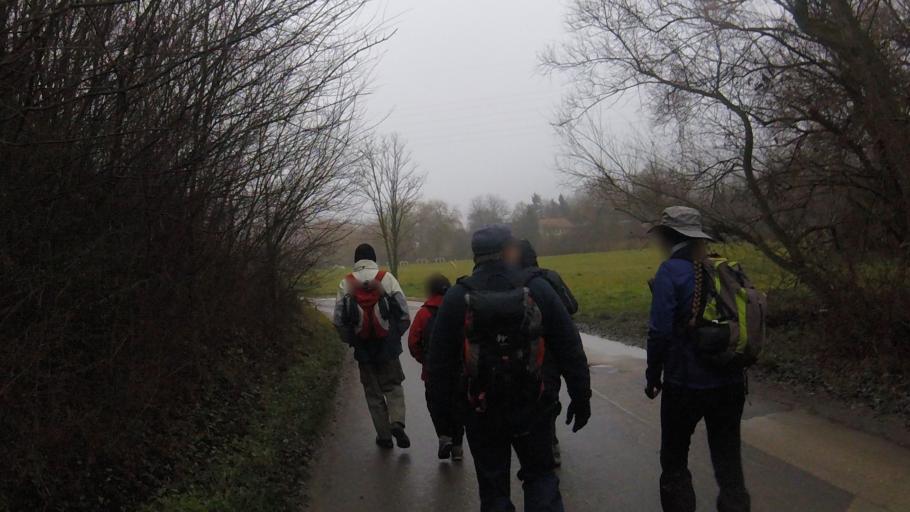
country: HU
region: Pest
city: Biatorbagy
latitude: 47.4709
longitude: 18.8349
